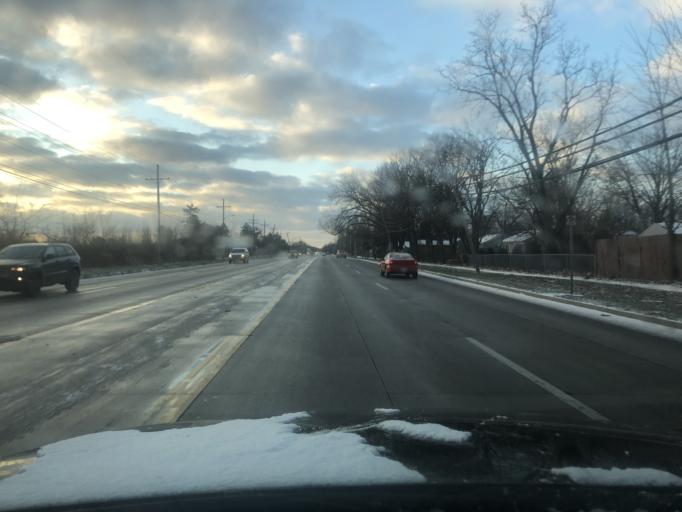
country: US
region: Michigan
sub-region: Wayne County
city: Garden City
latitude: 42.2947
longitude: -83.3492
